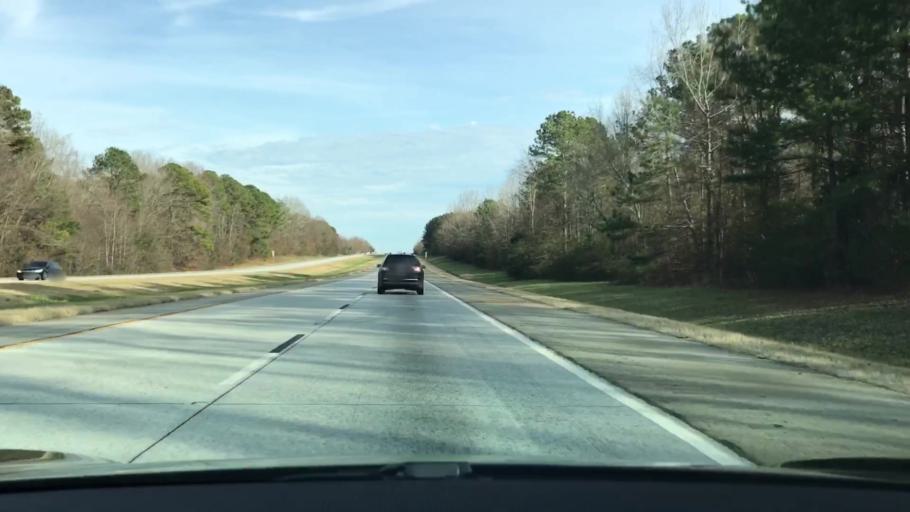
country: US
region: Georgia
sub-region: Morgan County
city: Madison
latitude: 33.5545
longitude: -83.4238
